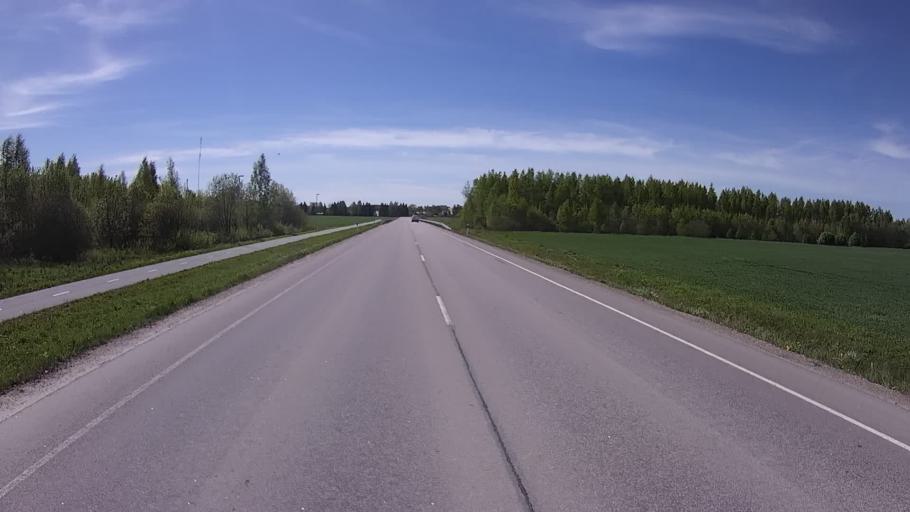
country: EE
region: Polvamaa
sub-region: Polva linn
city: Polva
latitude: 58.0778
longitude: 27.0891
